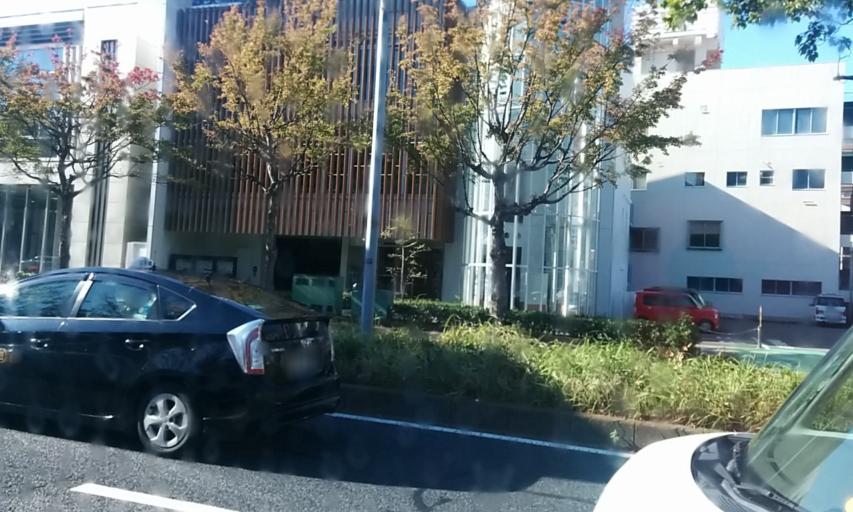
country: JP
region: Wakayama
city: Wakayama-shi
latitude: 34.2275
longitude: 135.1692
